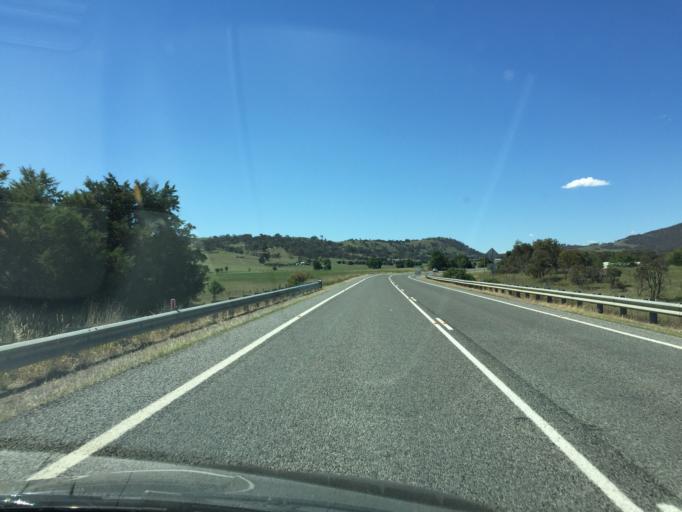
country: AU
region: Australian Capital Territory
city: Macarthur
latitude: -35.7061
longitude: 149.1583
